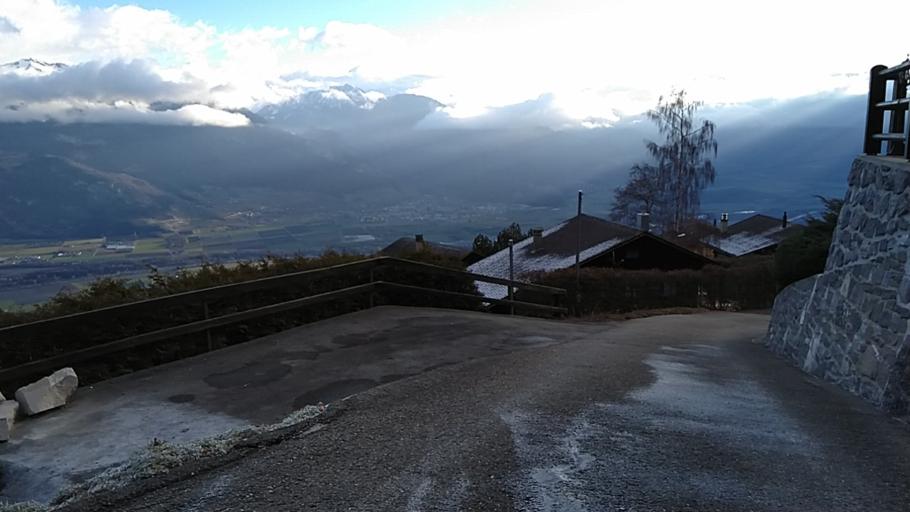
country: CH
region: Valais
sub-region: Monthey District
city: Vouvry
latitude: 46.3214
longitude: 6.8754
